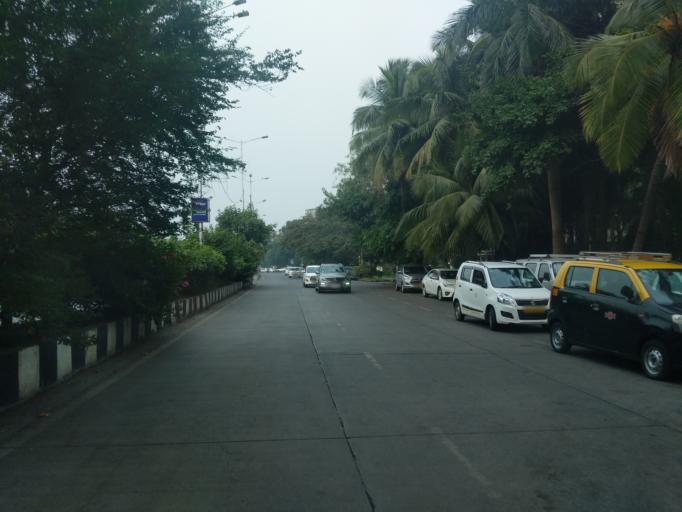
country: IN
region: Maharashtra
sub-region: Raigarh
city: Uran
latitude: 18.9282
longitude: 72.8210
